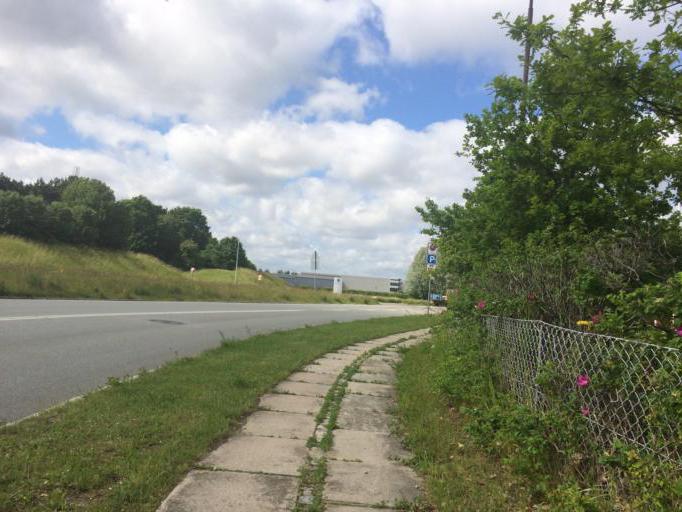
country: DK
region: Capital Region
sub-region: Hvidovre Kommune
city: Hvidovre
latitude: 55.6074
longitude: 12.4528
